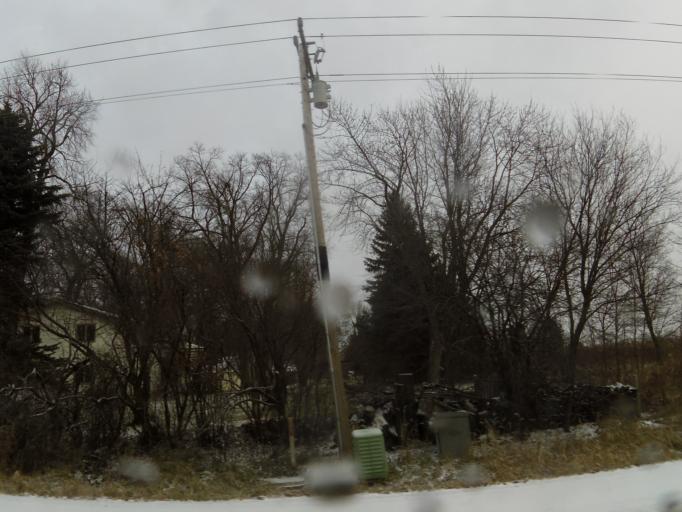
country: US
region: Minnesota
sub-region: Scott County
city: Prior Lake
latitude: 44.6922
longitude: -93.4603
